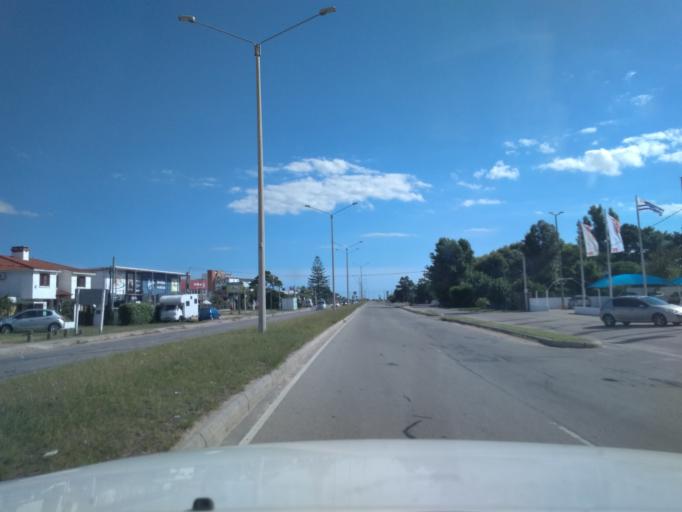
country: UY
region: Canelones
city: Barra de Carrasco
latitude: -34.8699
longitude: -56.0219
